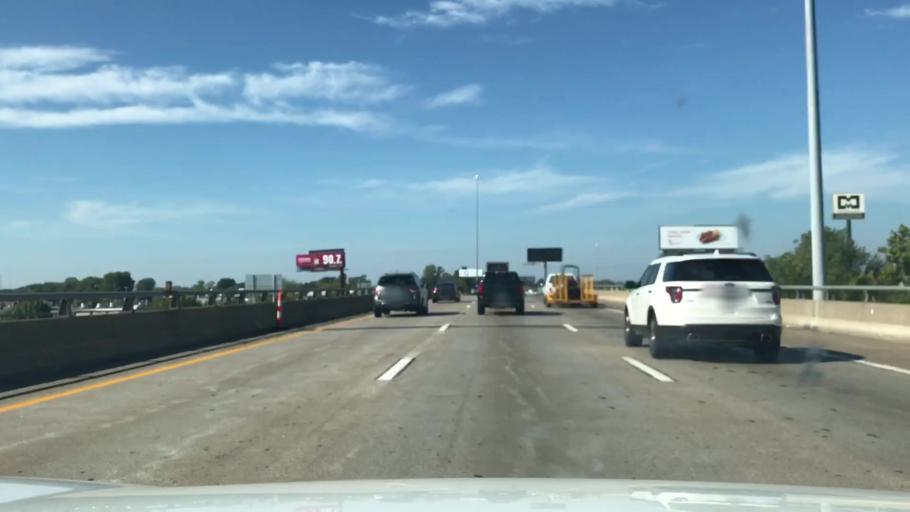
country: US
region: Missouri
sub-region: City of Saint Louis
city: St. Louis
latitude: 38.6318
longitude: -90.2463
